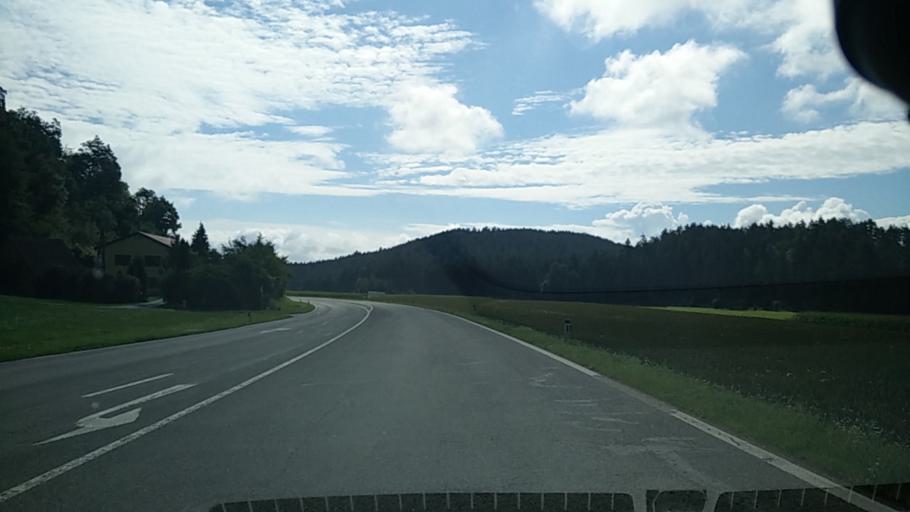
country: AT
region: Carinthia
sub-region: Politischer Bezirk Volkermarkt
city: Voelkermarkt
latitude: 46.6535
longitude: 14.5551
